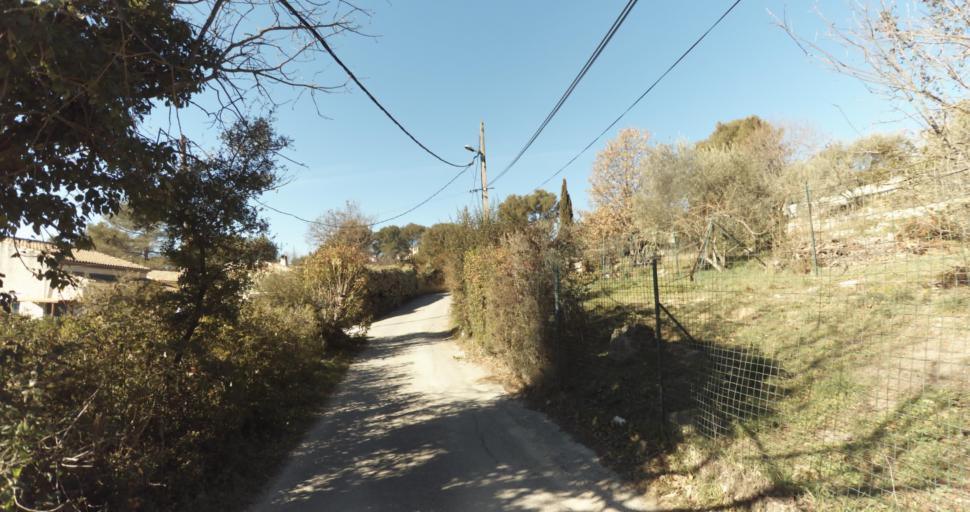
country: FR
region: Provence-Alpes-Cote d'Azur
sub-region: Departement des Bouches-du-Rhone
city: Peypin
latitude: 43.3872
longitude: 5.5834
